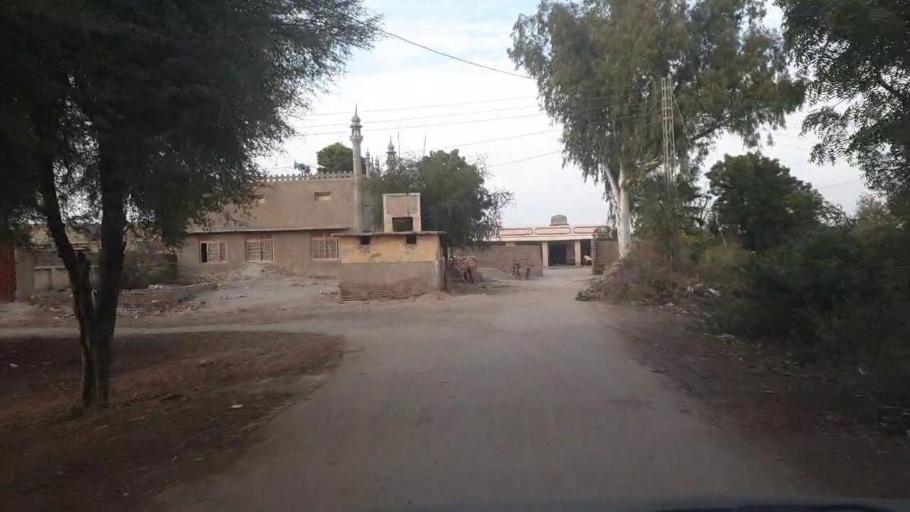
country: PK
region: Sindh
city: Shahpur Chakar
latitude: 26.1459
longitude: 68.6295
